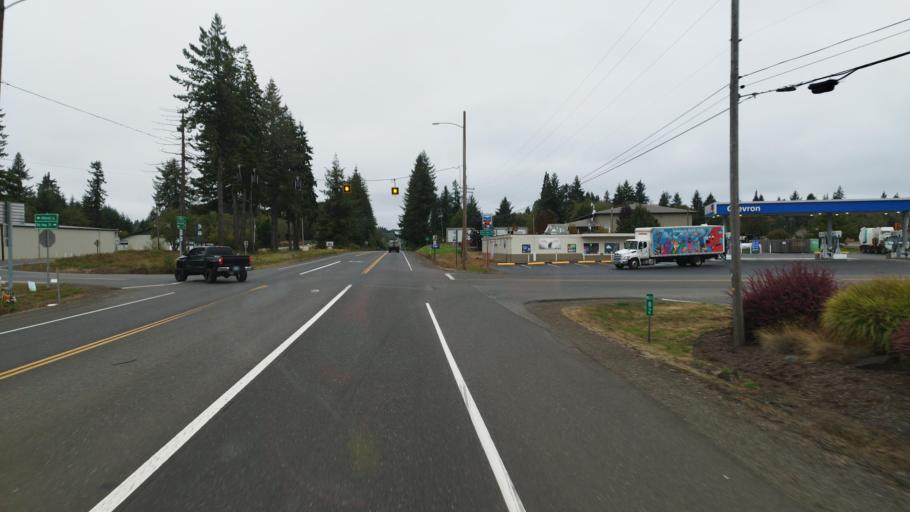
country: US
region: Washington
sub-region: Wahkiakum County
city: Cathlamet
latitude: 46.1683
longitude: -123.5811
